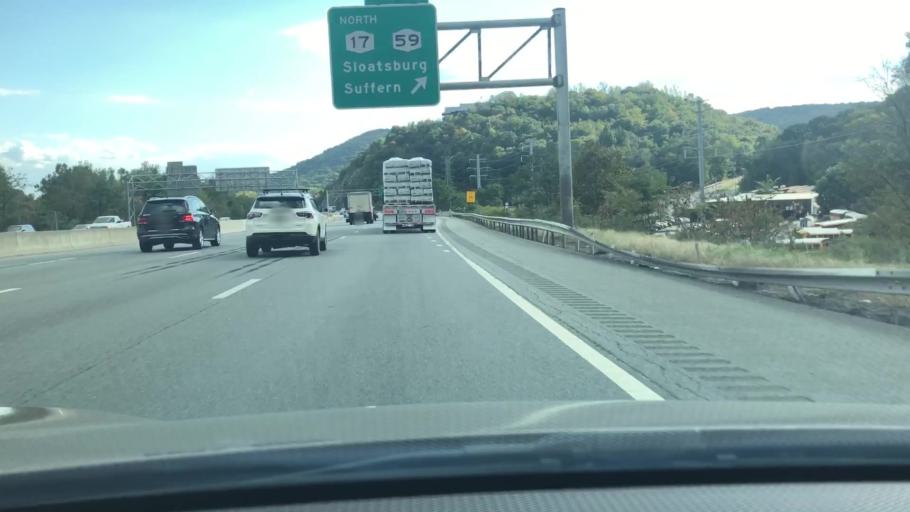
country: US
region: New York
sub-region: Rockland County
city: Suffern
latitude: 41.1349
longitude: -74.1685
